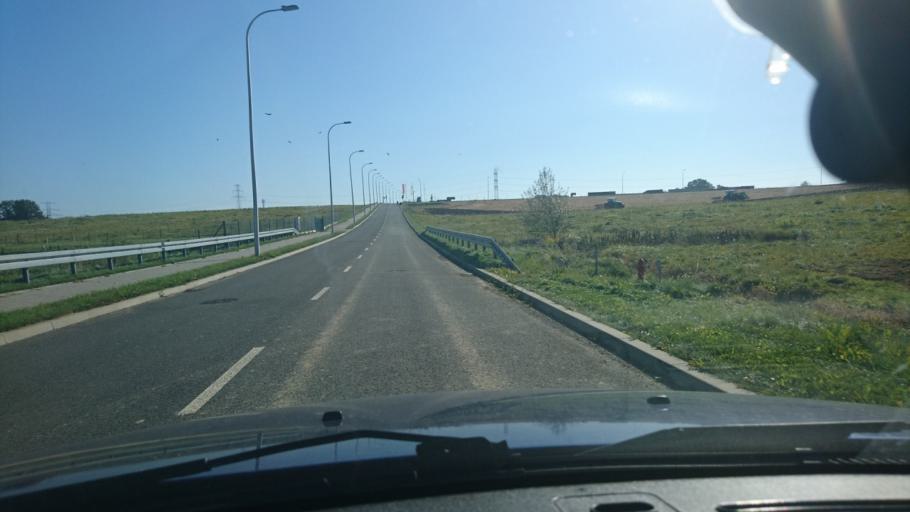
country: PL
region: Silesian Voivodeship
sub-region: Powiat bielski
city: Bronow
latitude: 49.8643
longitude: 18.9290
